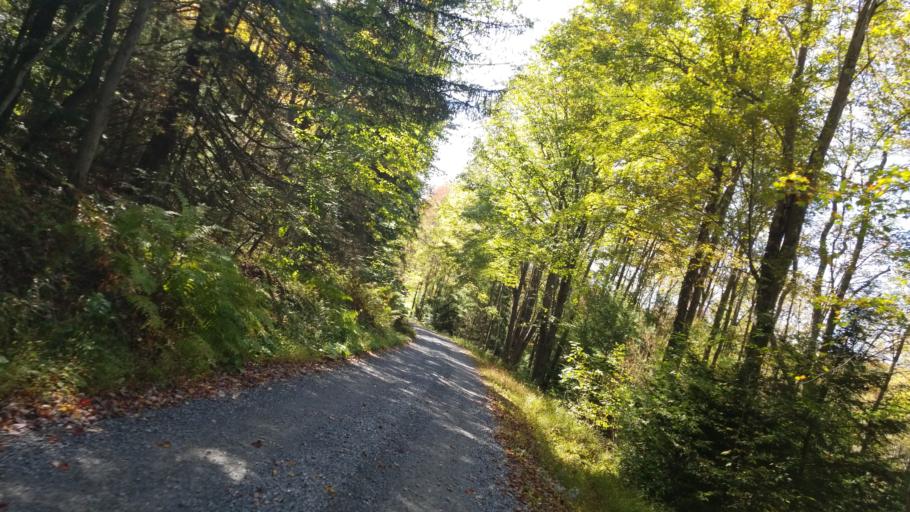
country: US
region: Pennsylvania
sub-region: Clearfield County
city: Clearfield
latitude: 41.1868
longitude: -78.5098
